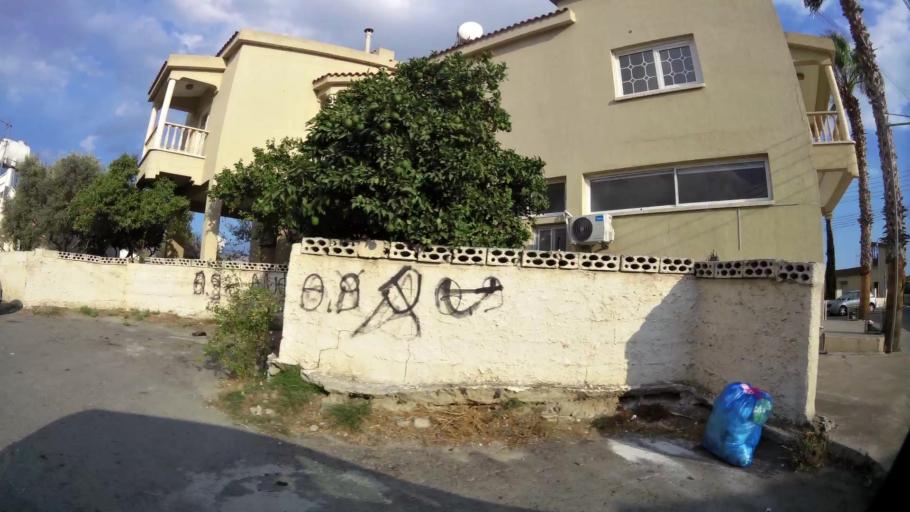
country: CY
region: Larnaka
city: Dhromolaxia
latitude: 34.8768
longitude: 33.5865
